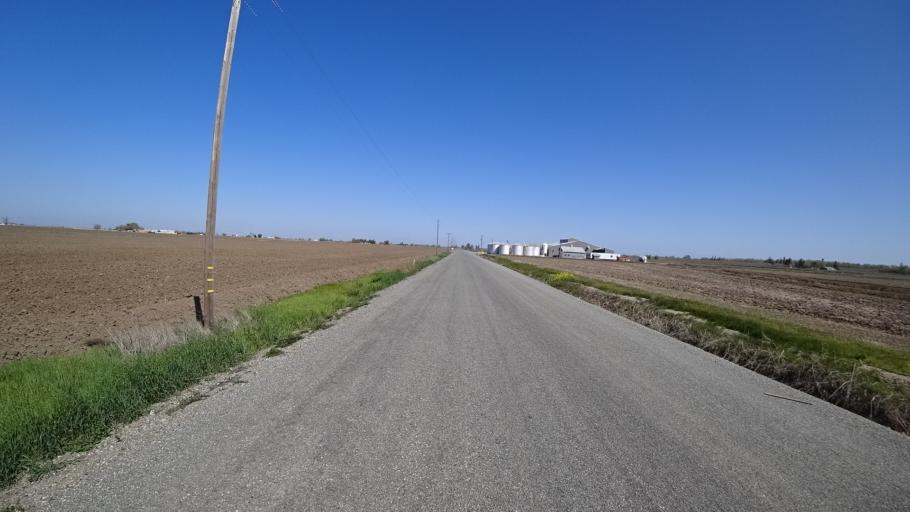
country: US
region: California
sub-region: Glenn County
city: Willows
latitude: 39.4377
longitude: -122.0320
